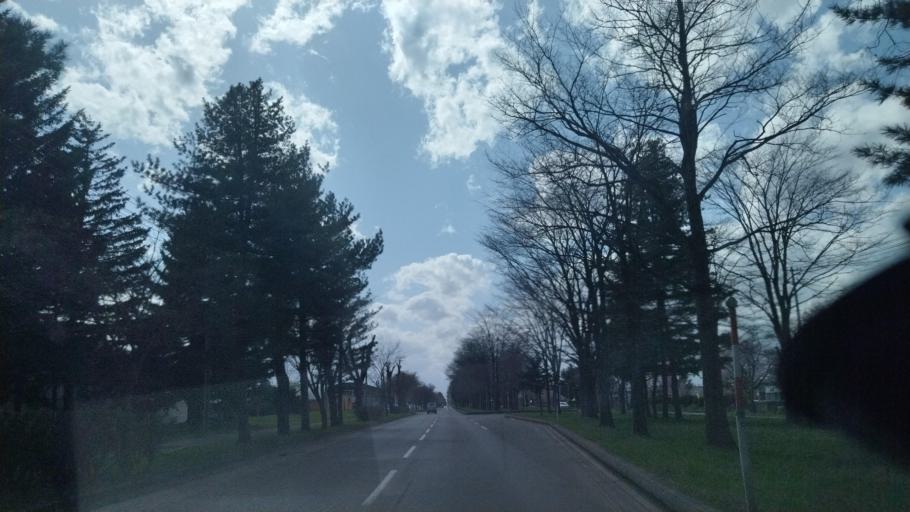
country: JP
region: Hokkaido
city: Obihiro
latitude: 42.9299
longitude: 143.1400
